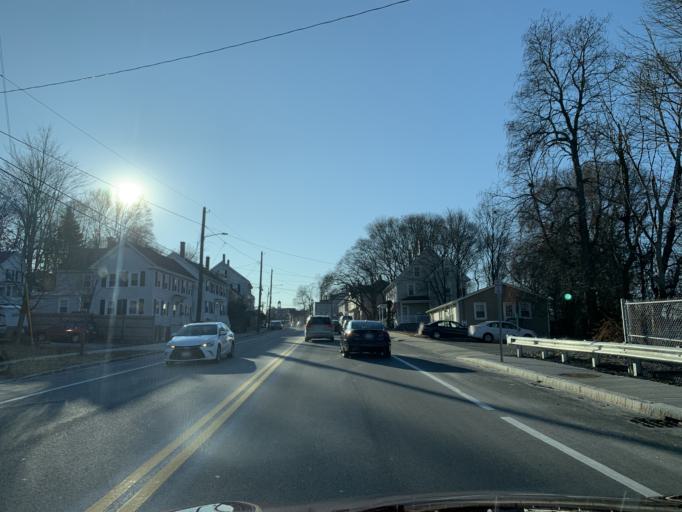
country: US
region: Massachusetts
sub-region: Essex County
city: Andover
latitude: 42.6604
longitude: -71.1436
